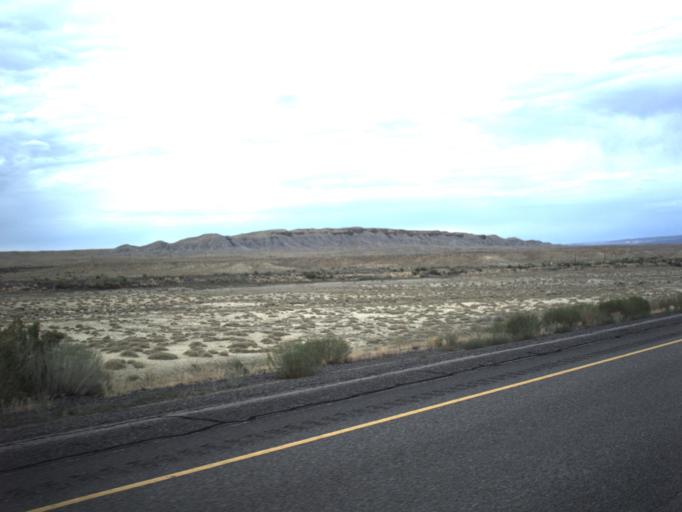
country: US
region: Utah
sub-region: Grand County
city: Moab
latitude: 38.9376
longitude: -109.4906
